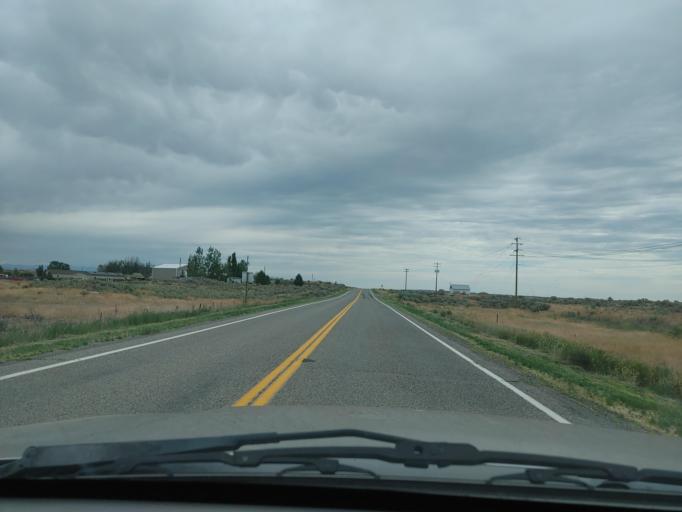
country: US
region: Idaho
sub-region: Lincoln County
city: Shoshone
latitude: 43.0531
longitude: -114.1385
